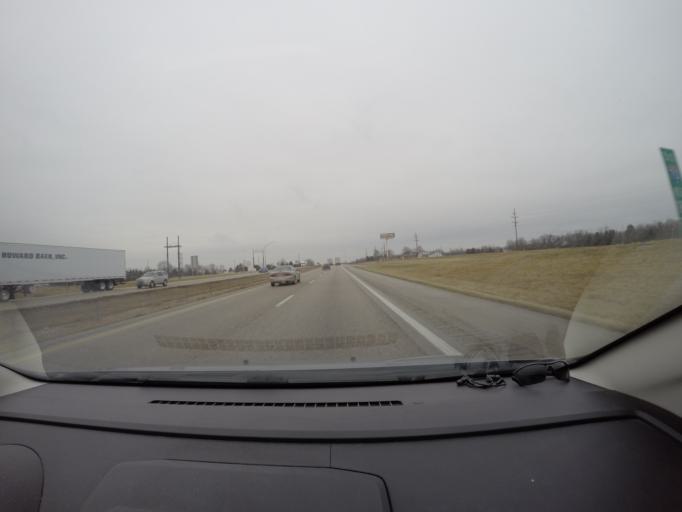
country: US
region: Missouri
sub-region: Montgomery County
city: Montgomery City
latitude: 38.8730
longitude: -91.3719
